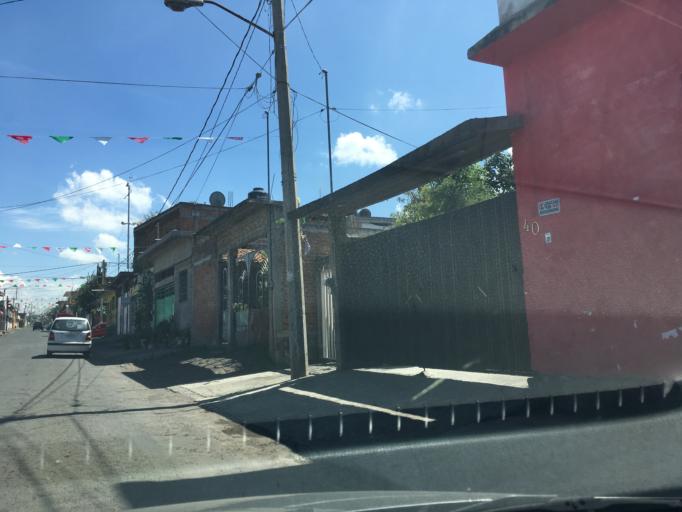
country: MX
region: Michoacan
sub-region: Morelia
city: Morelos
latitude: 19.6508
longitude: -101.2417
